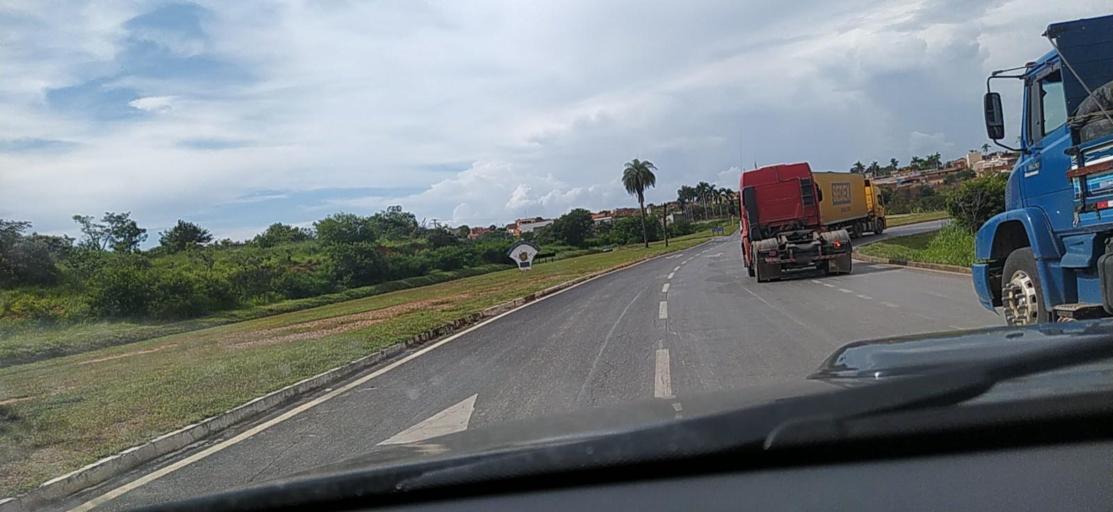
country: BR
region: Minas Gerais
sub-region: Montes Claros
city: Montes Claros
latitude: -16.7518
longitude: -43.8458
